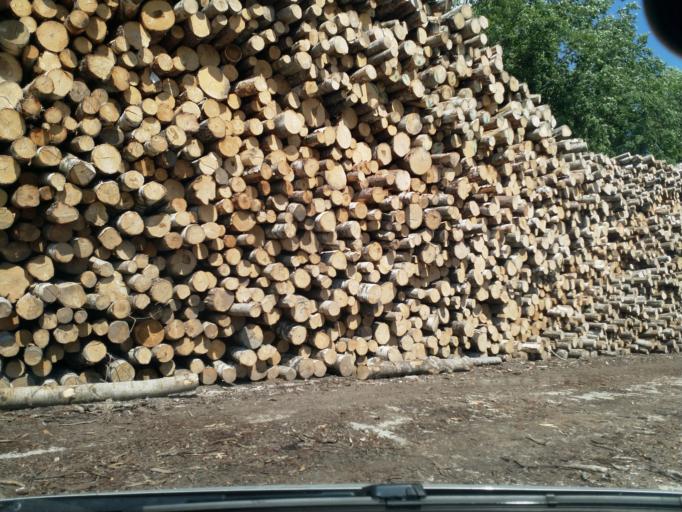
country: LV
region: Kuldigas Rajons
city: Kuldiga
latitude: 56.9682
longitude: 21.9221
